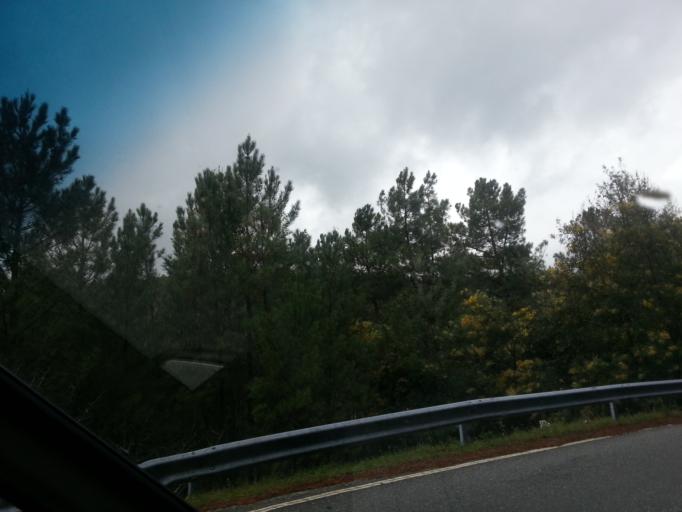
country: PT
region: Guarda
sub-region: Fornos de Algodres
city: Fornos de Algodres
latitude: 40.6096
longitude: -7.5760
